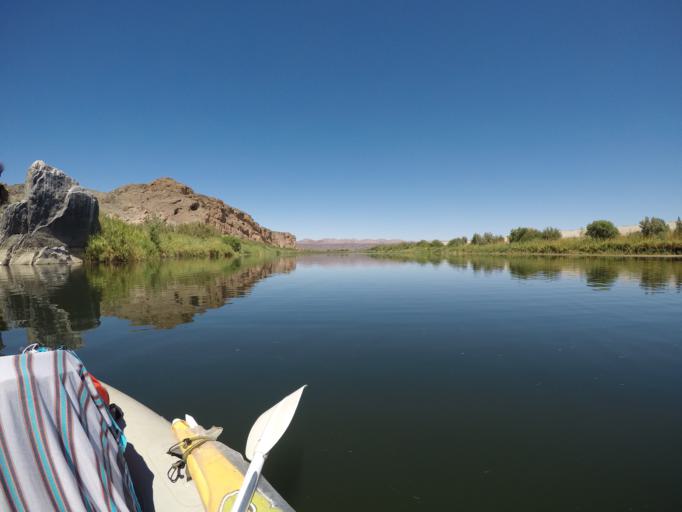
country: ZA
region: Northern Cape
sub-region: Namakwa District Municipality
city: Port Nolloth
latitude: -28.7015
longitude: 17.5405
